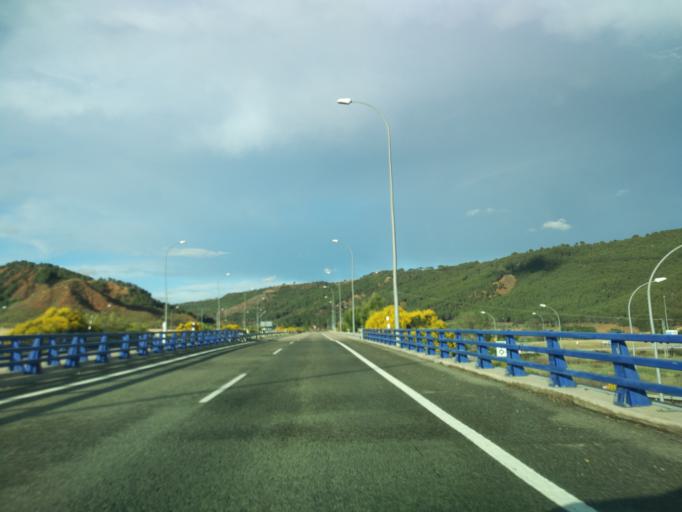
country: ES
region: Castille-La Mancha
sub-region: Provincia de Guadalajara
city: Tortola de Henares
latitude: 40.6616
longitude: -3.1195
